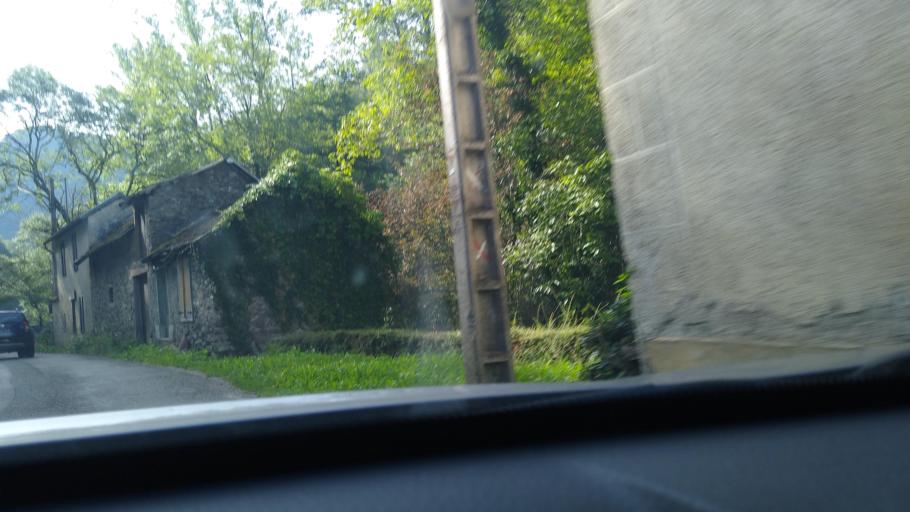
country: FR
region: Midi-Pyrenees
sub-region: Departement de l'Ariege
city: Saint-Girons
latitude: 42.8423
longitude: 1.1912
